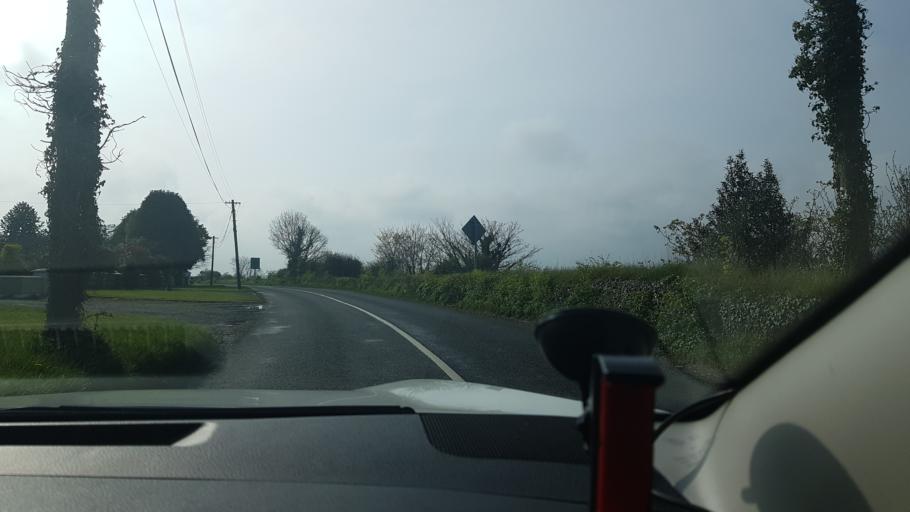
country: IE
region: Leinster
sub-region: Lu
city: Termonfeckin
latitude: 53.7212
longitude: -6.2863
